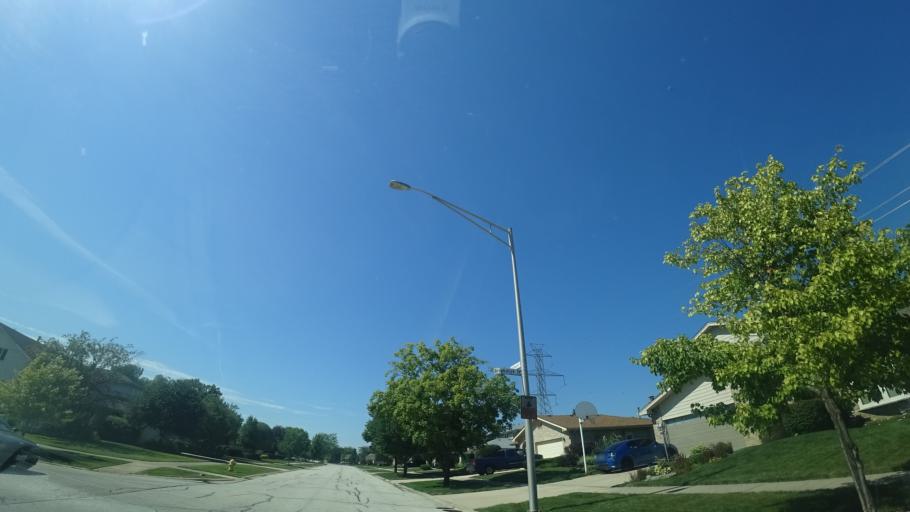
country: US
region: Illinois
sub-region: Will County
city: Mokena
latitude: 41.5721
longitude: -87.8969
